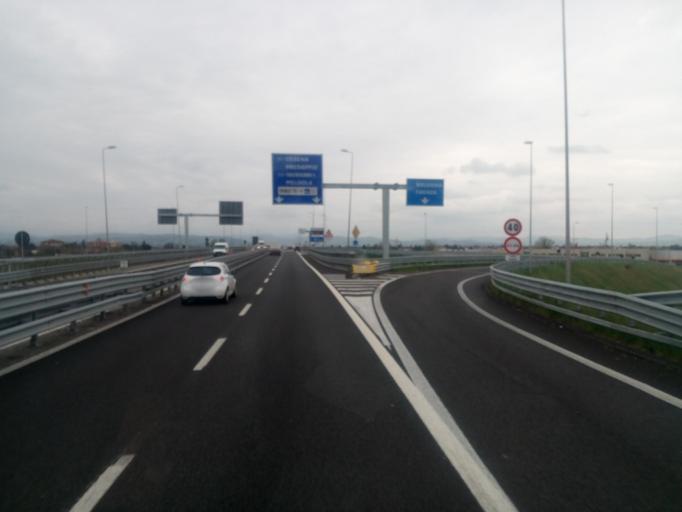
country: IT
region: Emilia-Romagna
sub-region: Forli-Cesena
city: Forli
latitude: 44.2189
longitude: 12.0784
